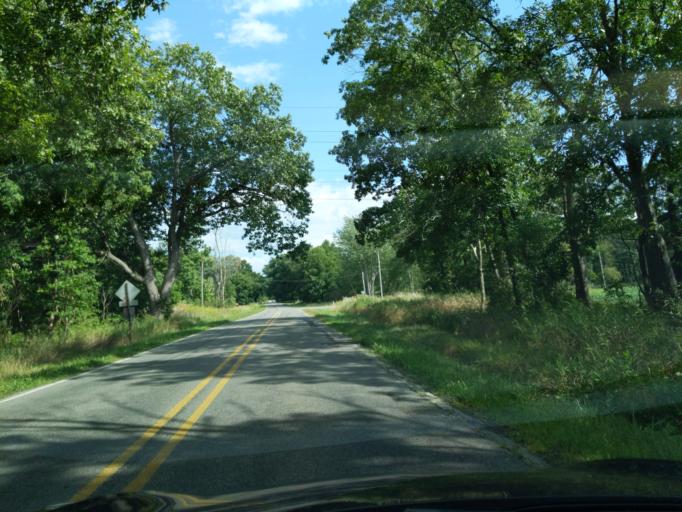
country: US
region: Michigan
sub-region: Jackson County
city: Spring Arbor
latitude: 42.3002
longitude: -84.5040
